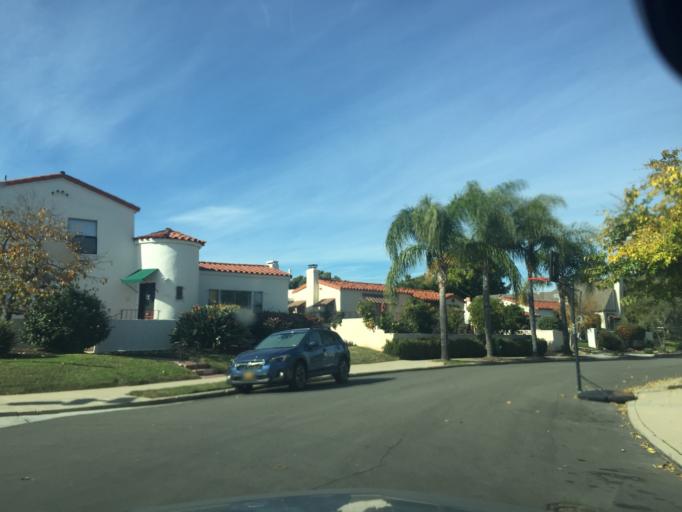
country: US
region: California
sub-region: San Diego County
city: Lemon Grove
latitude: 32.7665
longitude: -117.1008
